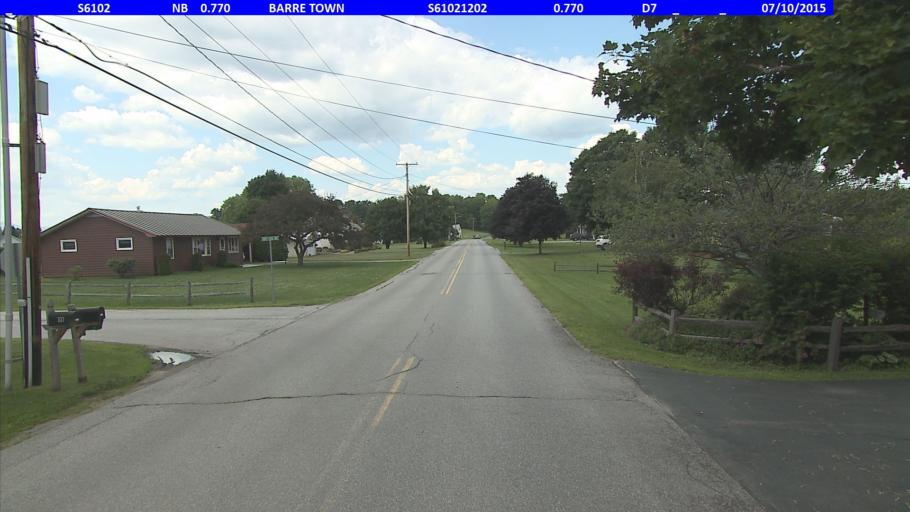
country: US
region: Vermont
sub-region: Washington County
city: Barre
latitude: 44.2232
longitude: -72.5095
